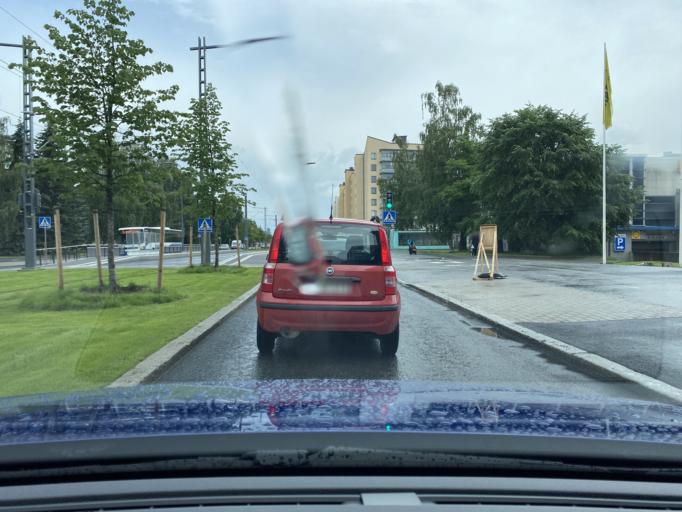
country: FI
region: Pirkanmaa
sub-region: Tampere
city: Tampere
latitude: 61.4947
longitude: 23.8110
